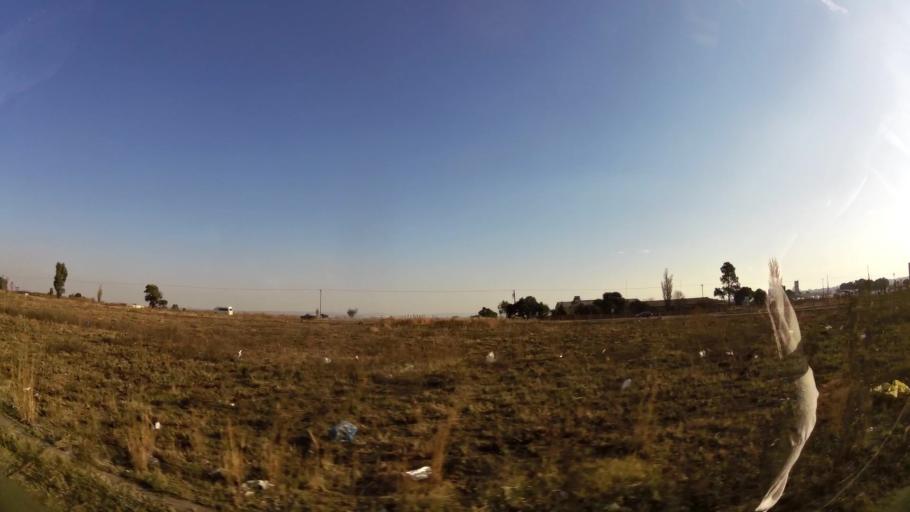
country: ZA
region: Gauteng
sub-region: West Rand District Municipality
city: Randfontein
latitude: -26.2047
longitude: 27.6901
